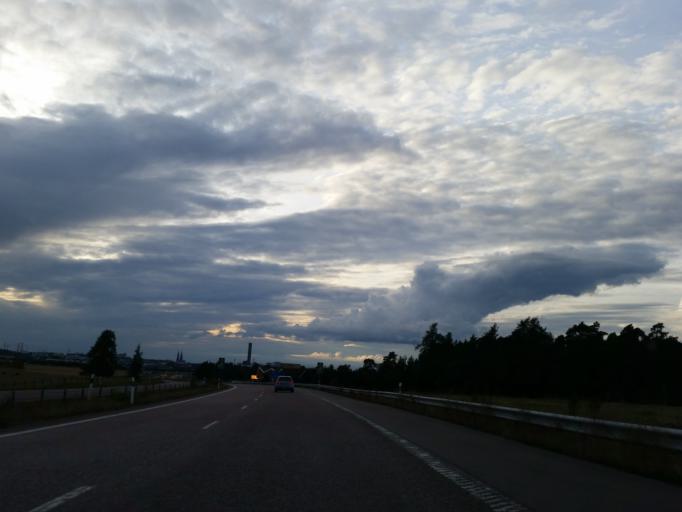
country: SE
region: Uppsala
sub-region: Uppsala Kommun
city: Saevja
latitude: 59.8412
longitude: 17.7197
